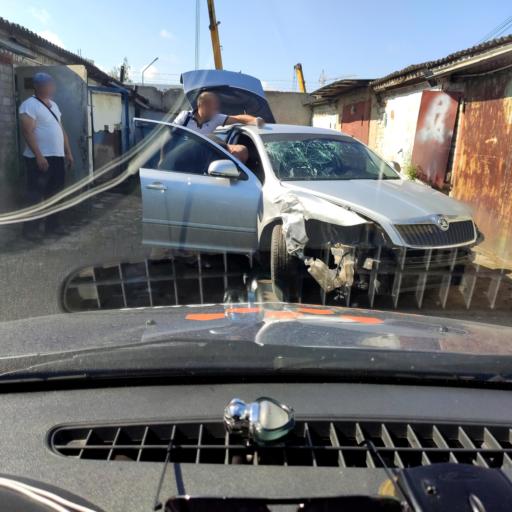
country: RU
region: Orjol
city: Orel
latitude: 52.9826
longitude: 36.0393
